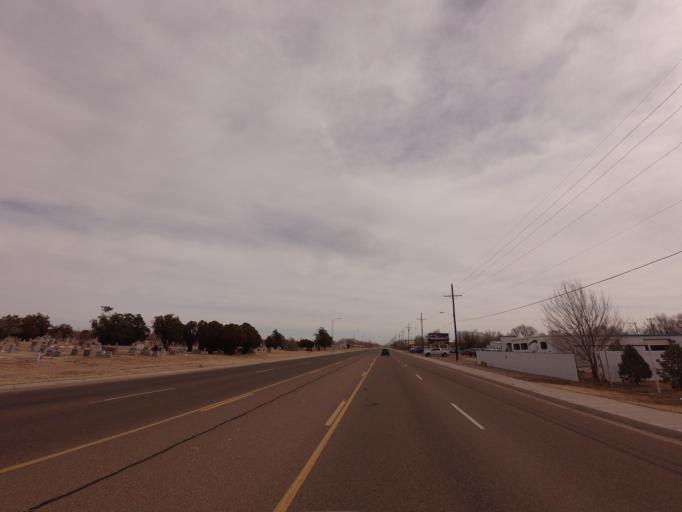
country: US
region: New Mexico
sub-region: Curry County
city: Clovis
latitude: 34.4046
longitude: -103.2431
